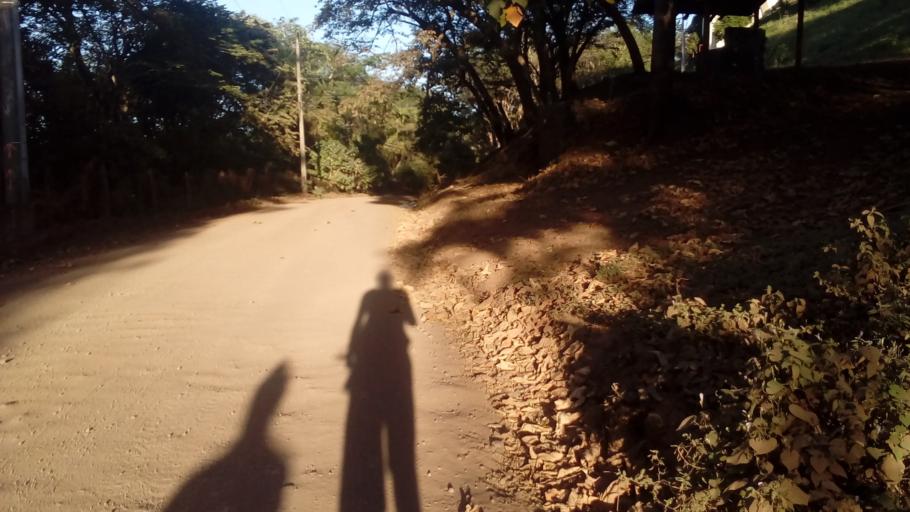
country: CR
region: Guanacaste
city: Sardinal
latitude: 10.3941
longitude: -85.8212
